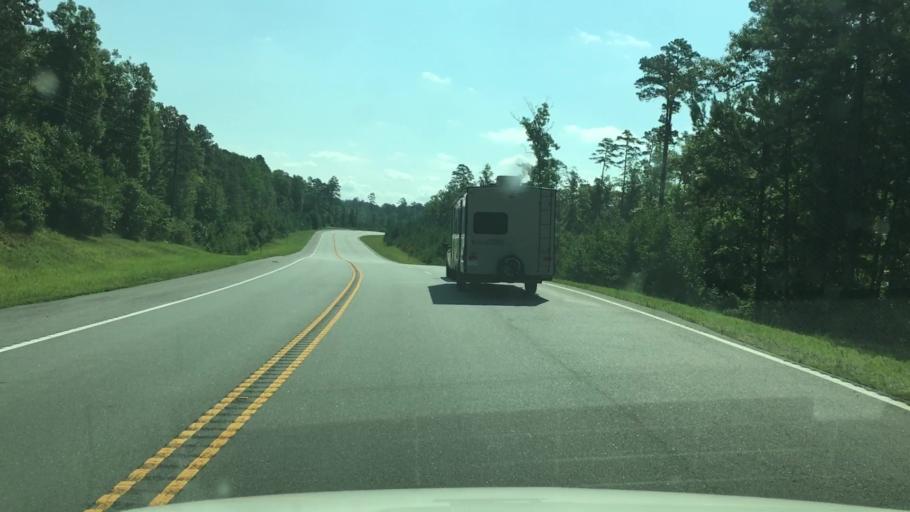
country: US
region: Arkansas
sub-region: Garland County
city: Rockwell
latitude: 34.5225
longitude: -93.3255
